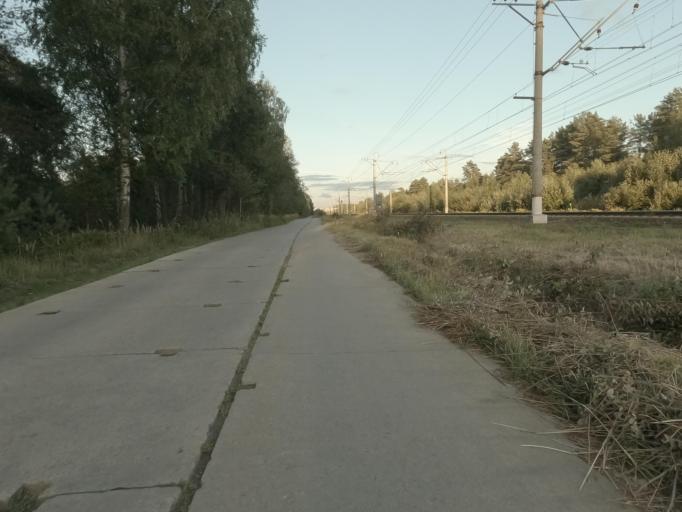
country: RU
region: Leningrad
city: Mga
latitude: 59.7618
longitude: 31.0034
